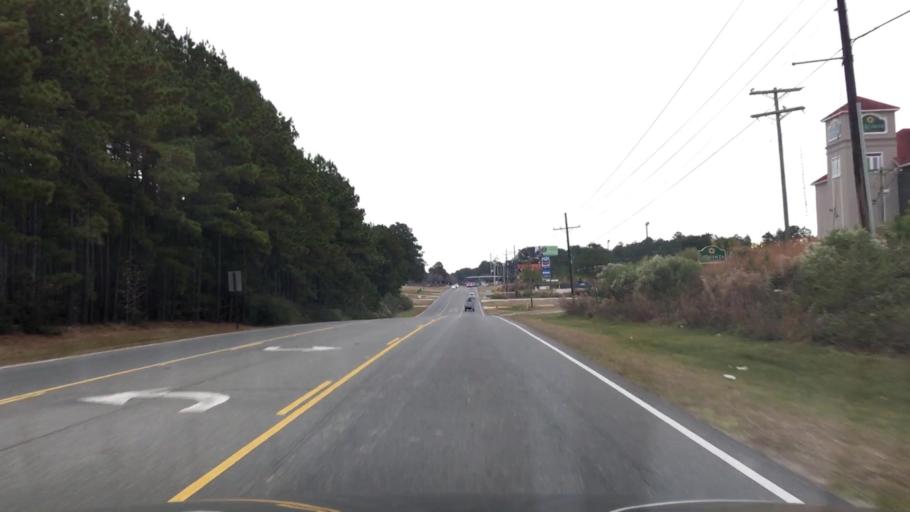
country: US
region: Louisiana
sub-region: Vernon Parish
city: Fort Polk South
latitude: 31.0546
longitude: -93.2399
